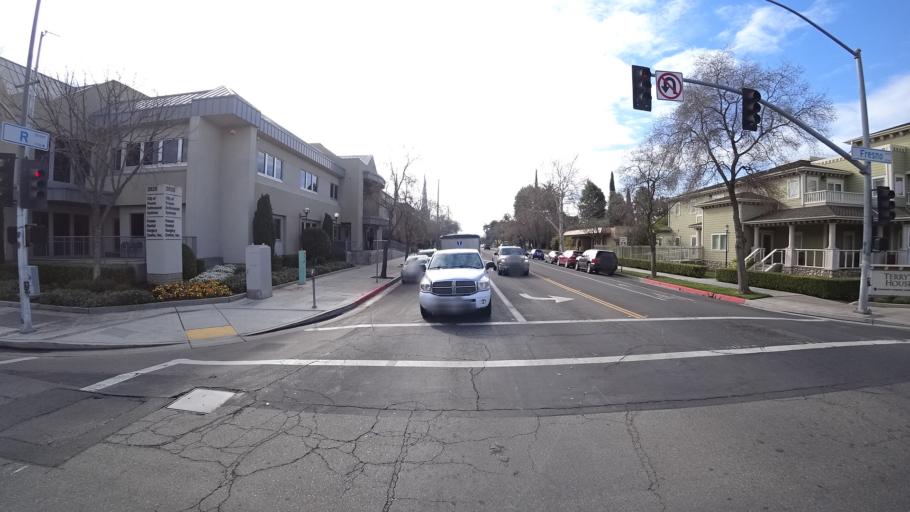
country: US
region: California
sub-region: Fresno County
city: Fresno
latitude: 36.7417
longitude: -119.7841
